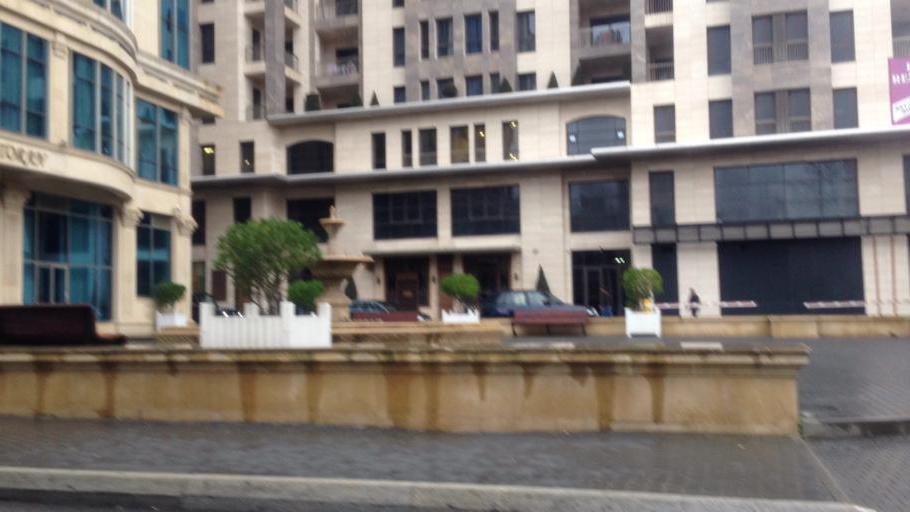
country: AZ
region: Baki
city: Baku
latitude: 40.3751
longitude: 49.8414
